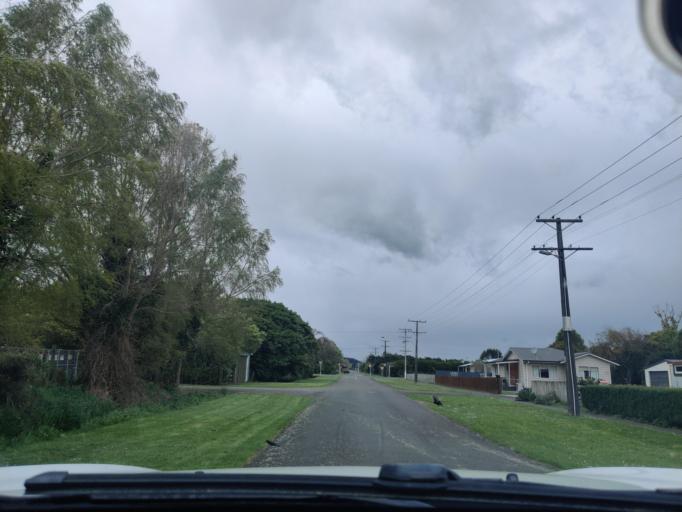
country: NZ
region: Manawatu-Wanganui
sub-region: Palmerston North City
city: Palmerston North
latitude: -40.3296
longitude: 175.8678
